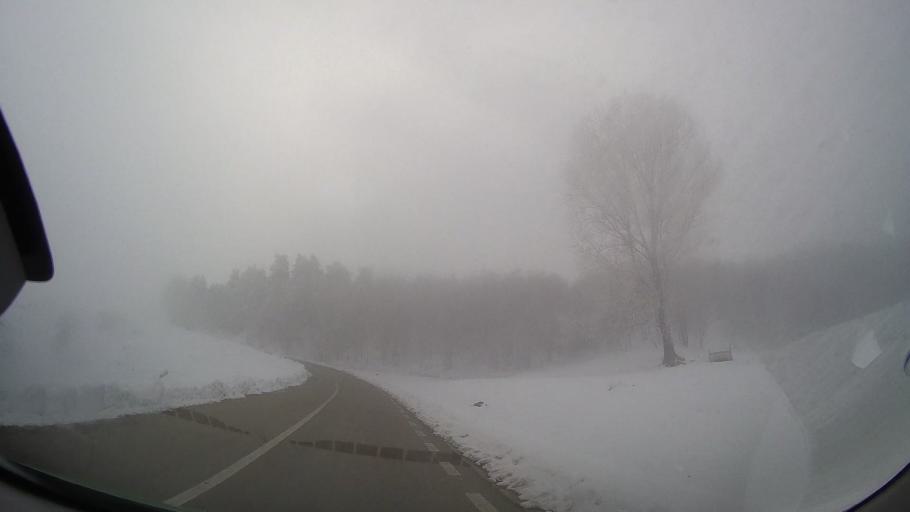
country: RO
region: Iasi
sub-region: Comuna Valea Seaca
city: Topile
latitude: 47.2688
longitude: 26.6700
